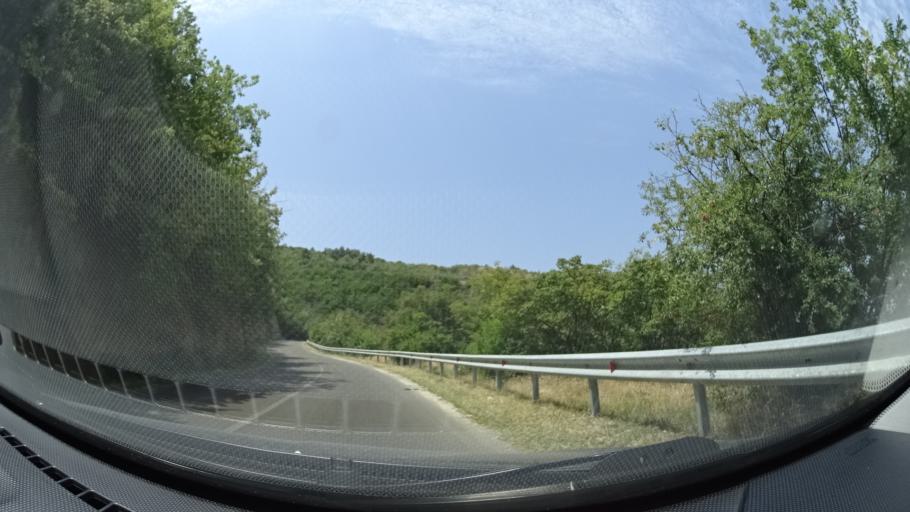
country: GE
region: Kakheti
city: Sighnaghi
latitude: 41.6225
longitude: 45.9329
